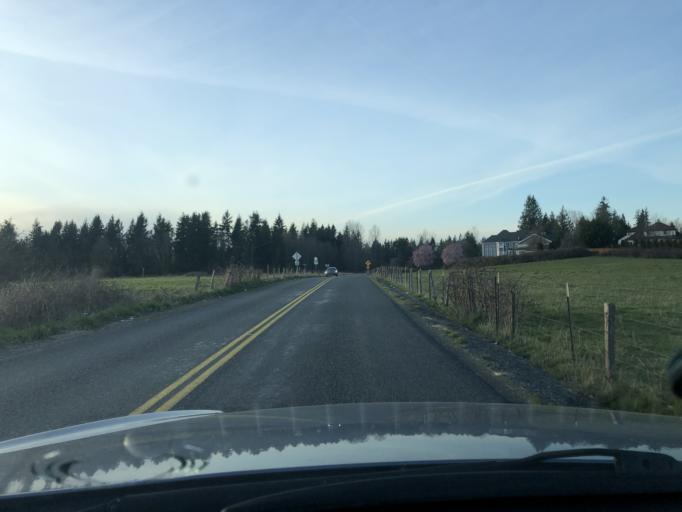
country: US
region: Washington
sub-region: Pierce County
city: Prairie Ridge
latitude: 47.2009
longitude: -122.1211
